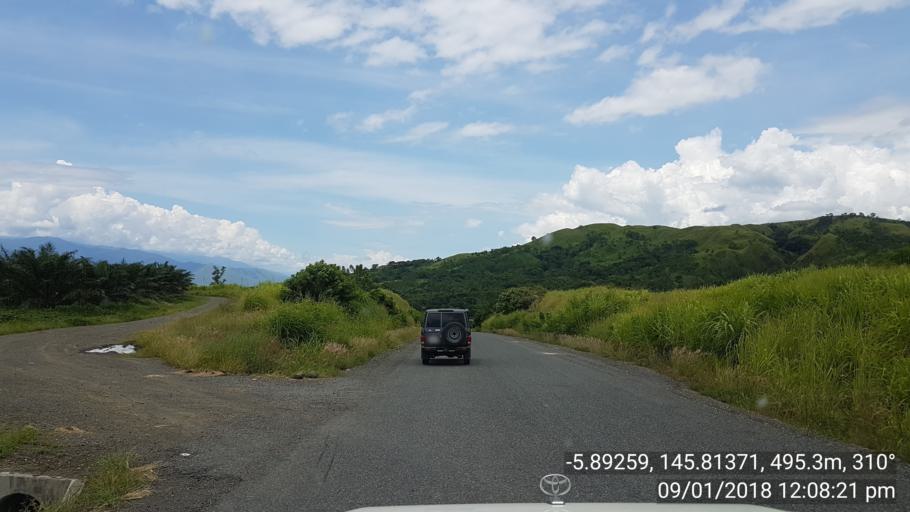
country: PG
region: Eastern Highlands
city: Kainantu
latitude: -5.8928
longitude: 145.8138
